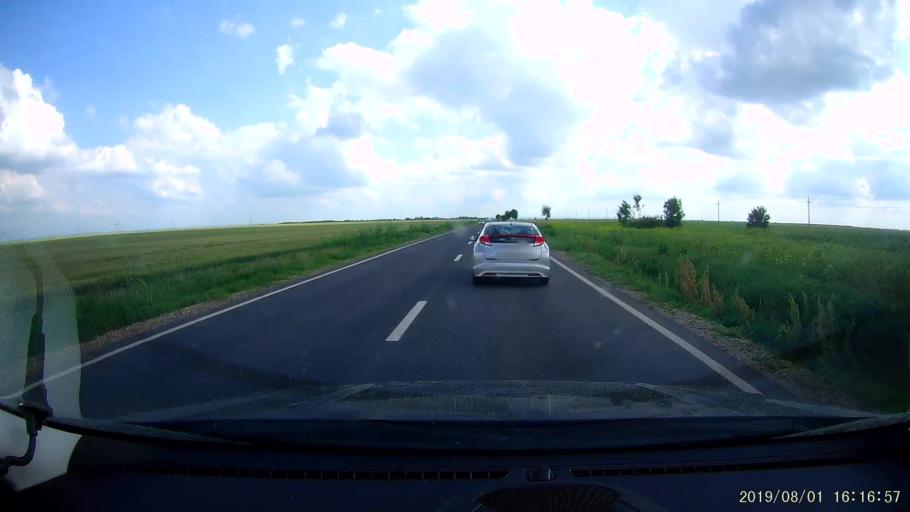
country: RO
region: Calarasi
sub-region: Comuna Stefan Voda
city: Stefan Voda
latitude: 44.3117
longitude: 27.3565
